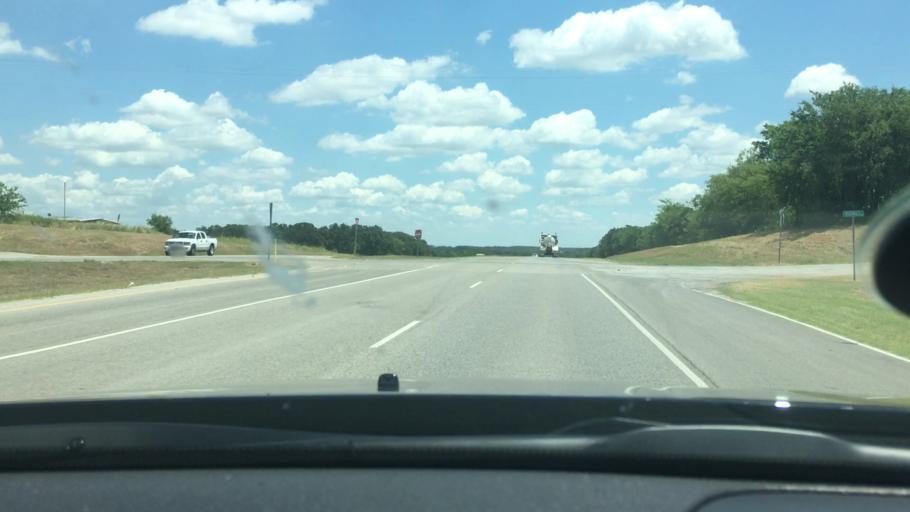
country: US
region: Oklahoma
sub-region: Carter County
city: Wilson
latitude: 34.1728
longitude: -97.3876
